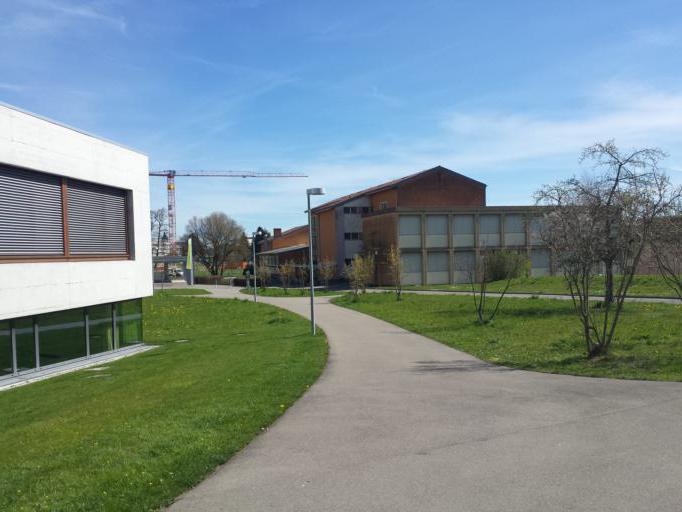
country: CH
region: Thurgau
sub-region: Arbon District
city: Romanshorn
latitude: 47.5677
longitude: 9.3714
